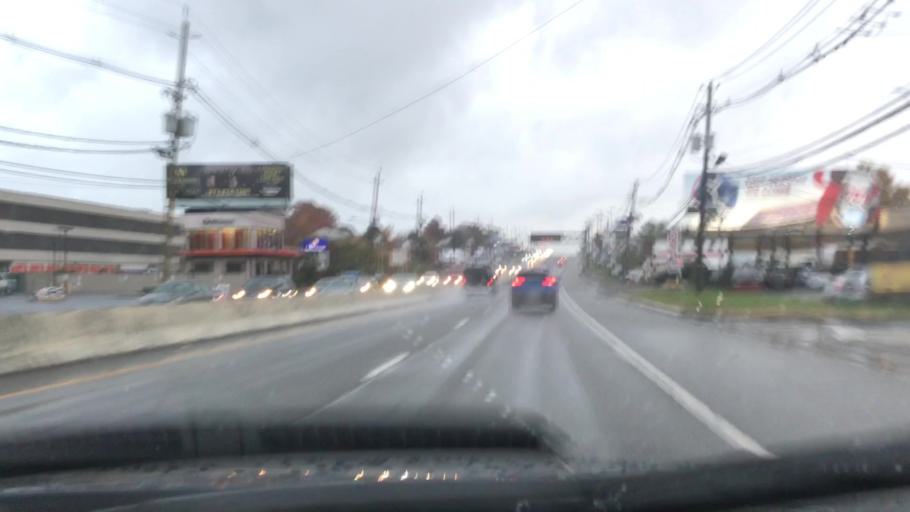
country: US
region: New Jersey
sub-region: Bergen County
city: Lodi
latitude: 40.8795
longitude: -74.0780
